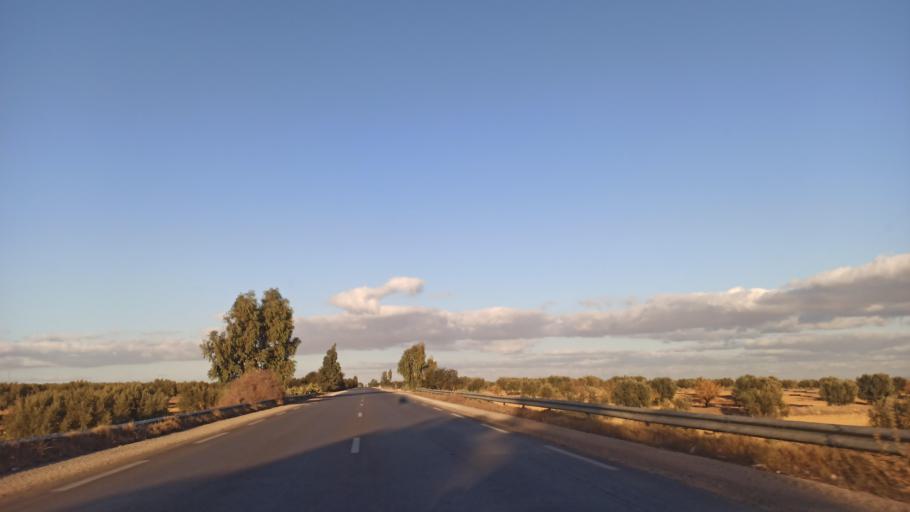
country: TN
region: Al Qayrawan
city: Sbikha
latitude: 35.8598
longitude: 10.2053
